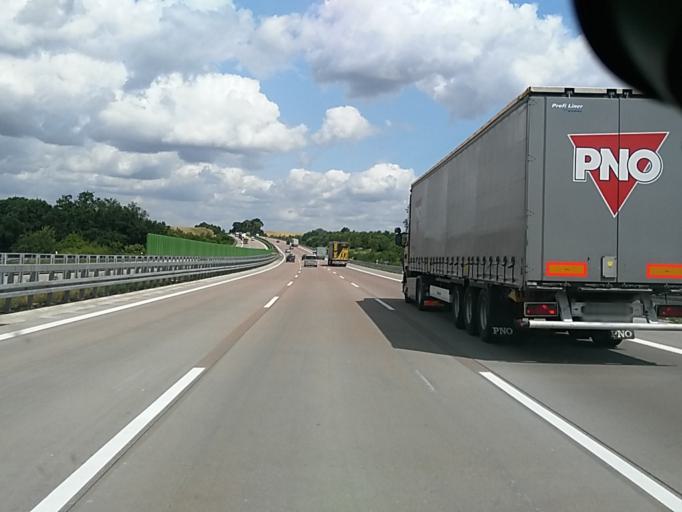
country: DE
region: Saxony-Anhalt
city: Osterfeld
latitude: 51.0634
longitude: 11.9521
